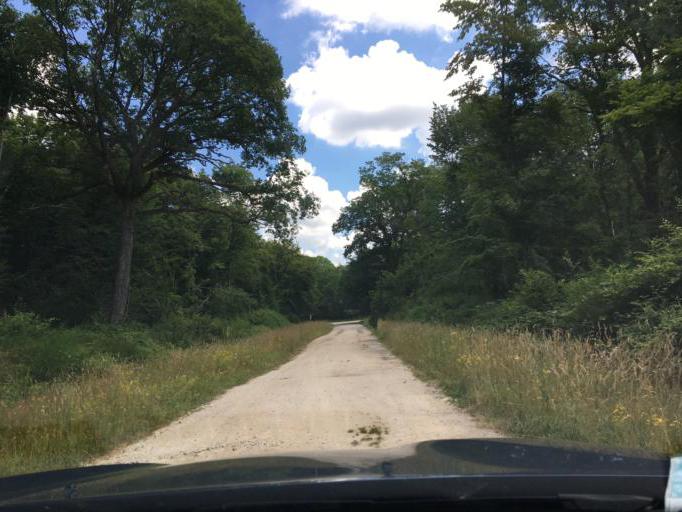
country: FR
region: Centre
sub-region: Departement du Loiret
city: Chanteau
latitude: 47.9841
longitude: 1.9256
